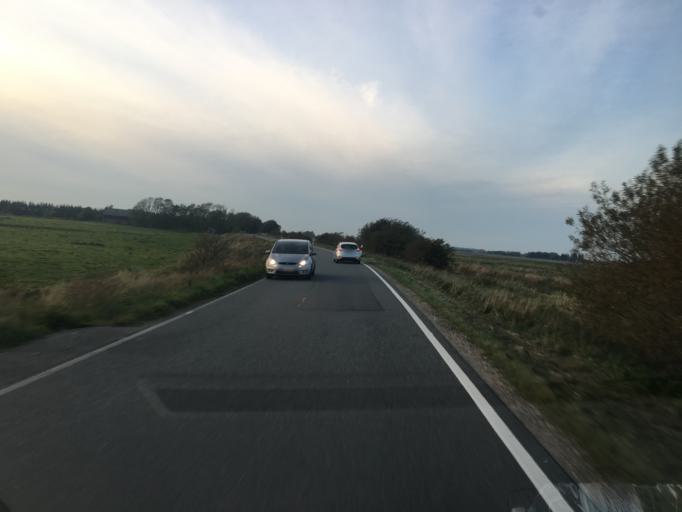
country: DE
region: Schleswig-Holstein
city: Aventoft
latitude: 54.8972
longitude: 8.8484
